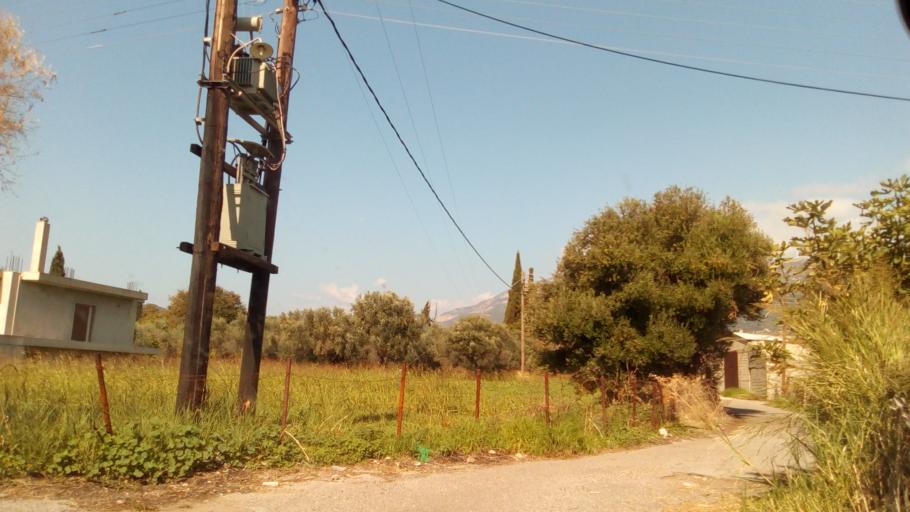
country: GR
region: West Greece
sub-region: Nomos Aitolias kai Akarnanias
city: Nafpaktos
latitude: 38.3814
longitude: 21.8080
